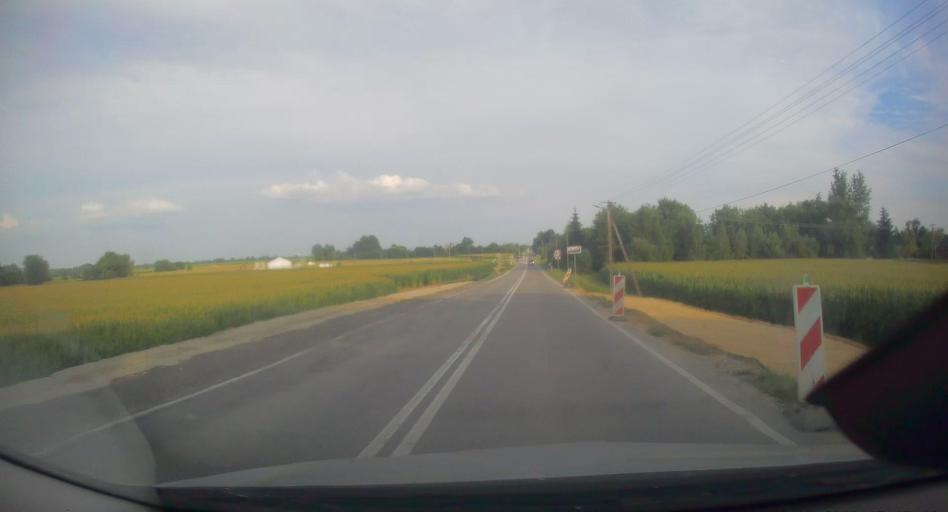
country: PL
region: Lesser Poland Voivodeship
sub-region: Powiat brzeski
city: Szczurowa
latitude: 50.1649
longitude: 20.5939
